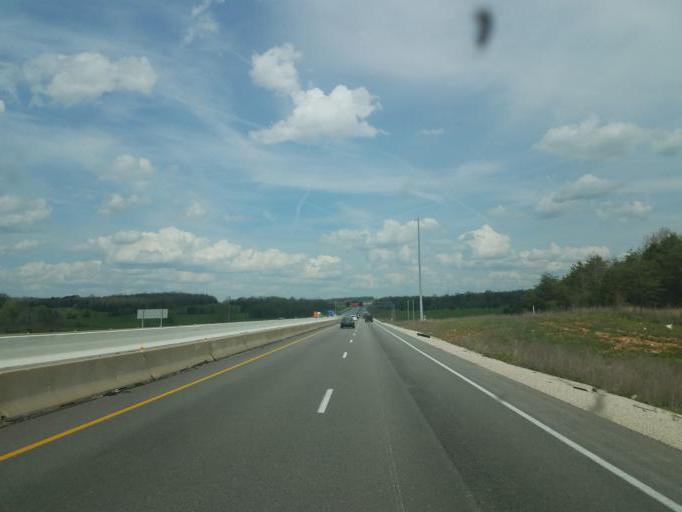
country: US
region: Kentucky
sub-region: Hart County
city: Munfordville
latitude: 37.4250
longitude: -85.8826
